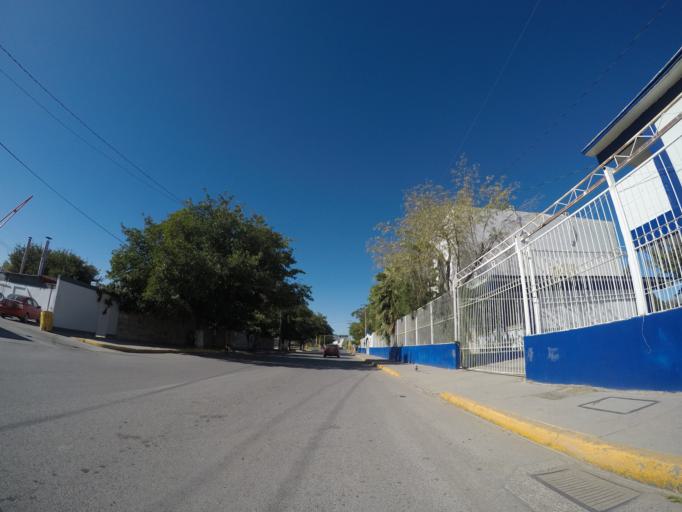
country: MX
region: Chihuahua
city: Ciudad Juarez
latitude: 31.7438
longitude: -106.4477
